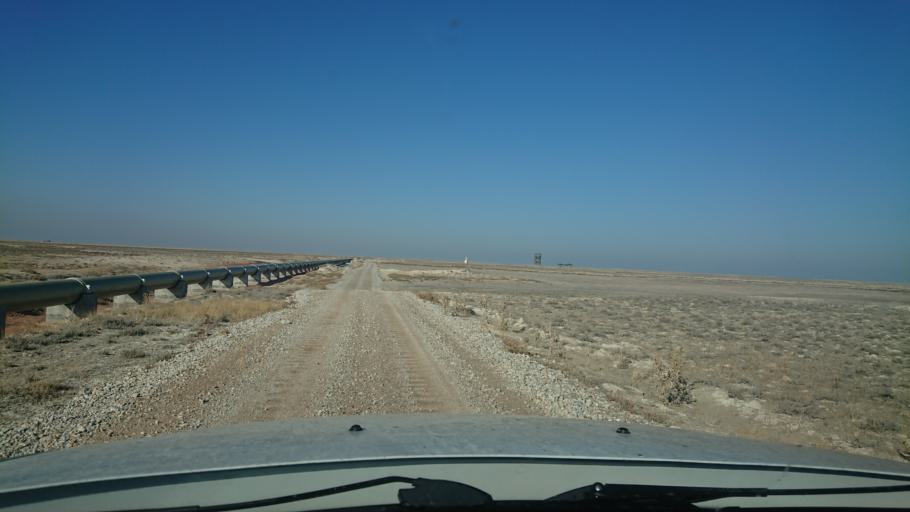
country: TR
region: Aksaray
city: Eskil
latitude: 38.4207
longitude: 33.5020
